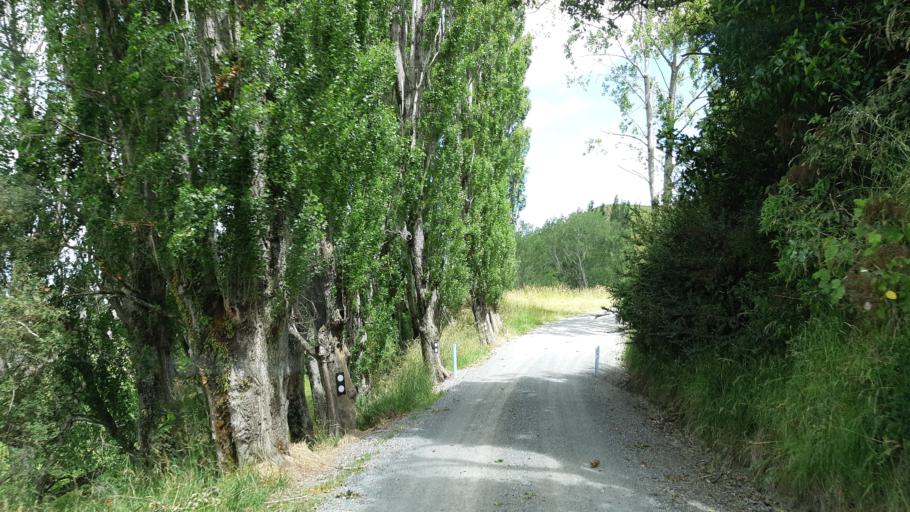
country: NZ
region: Manawatu-Wanganui
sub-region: Ruapehu District
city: Waiouru
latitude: -39.7799
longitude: 175.9224
